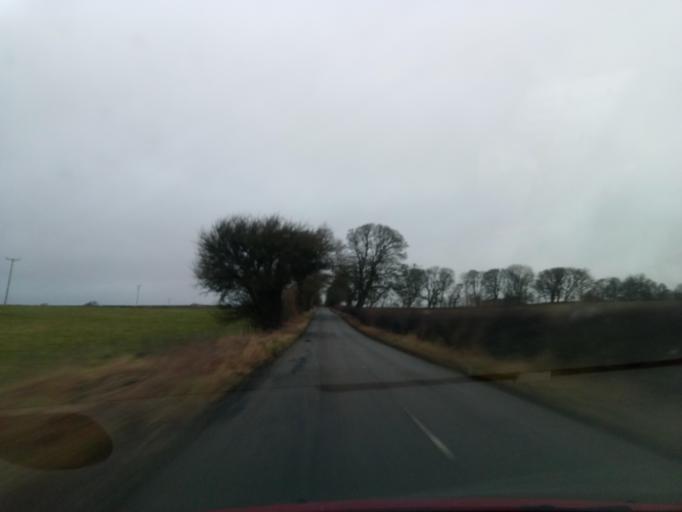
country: GB
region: England
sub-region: Northumberland
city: Rothley
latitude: 55.1925
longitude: -1.9713
